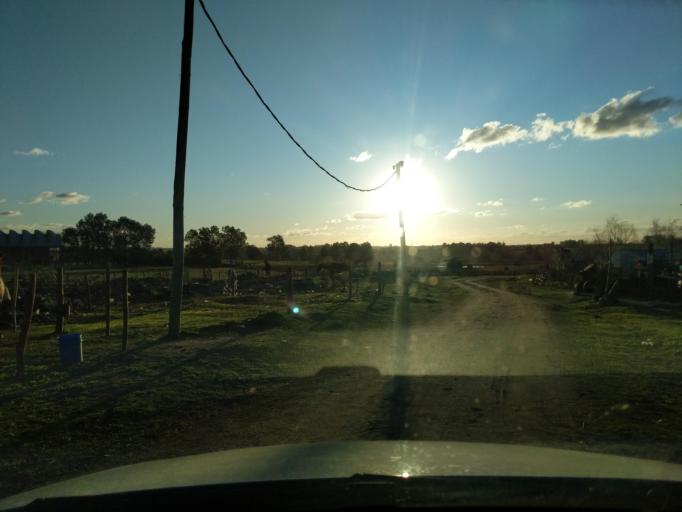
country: UY
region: Florida
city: Florida
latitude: -34.1055
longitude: -56.2373
